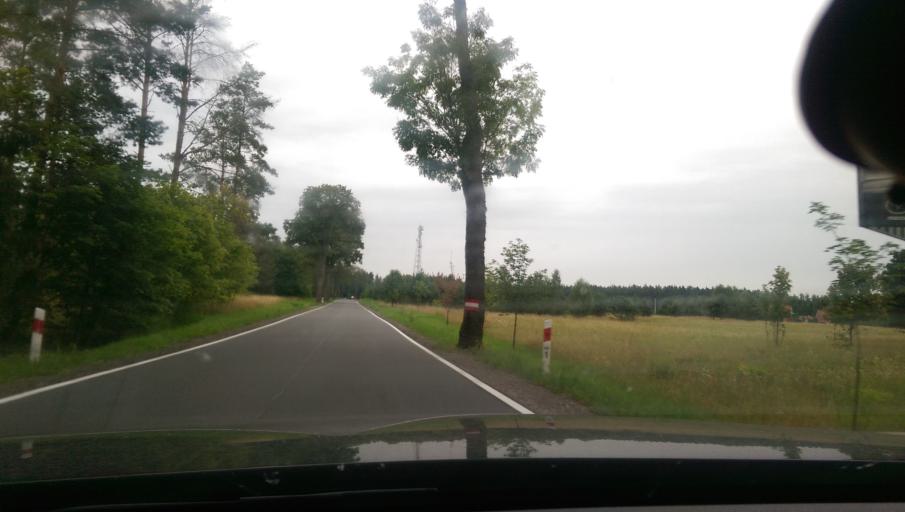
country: PL
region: Warmian-Masurian Voivodeship
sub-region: Powiat piski
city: Orzysz
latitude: 53.8443
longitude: 21.7892
